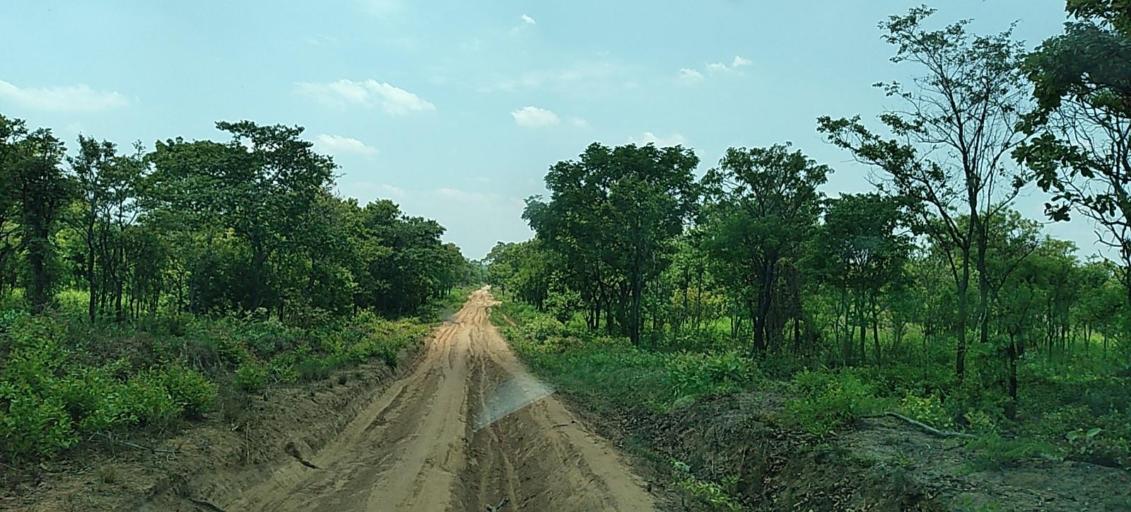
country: CD
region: Katanga
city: Kolwezi
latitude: -11.3477
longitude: 25.2153
